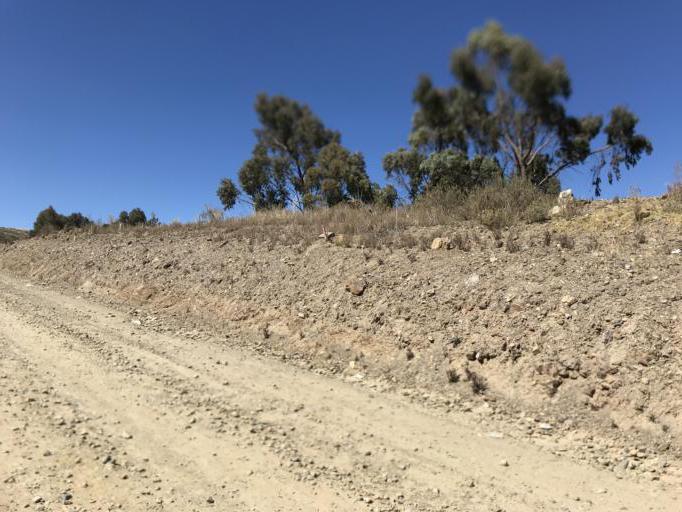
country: BO
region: La Paz
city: San Pablo
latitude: -16.1982
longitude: -68.8290
